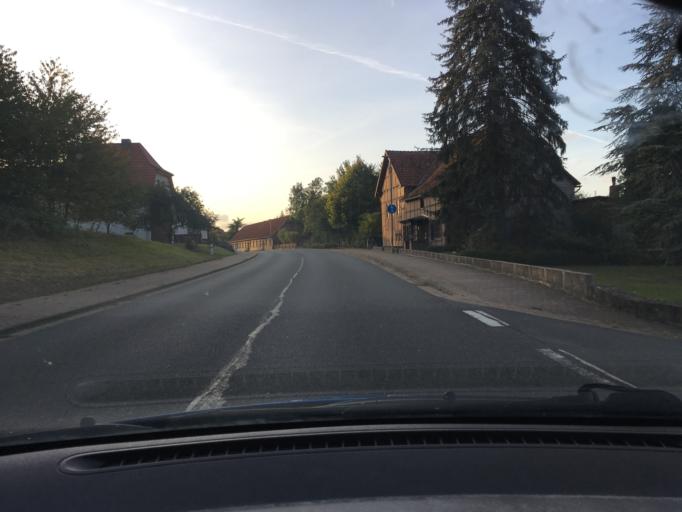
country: DE
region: Lower Saxony
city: Bad Munder am Deister
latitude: 52.2318
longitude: 9.4278
